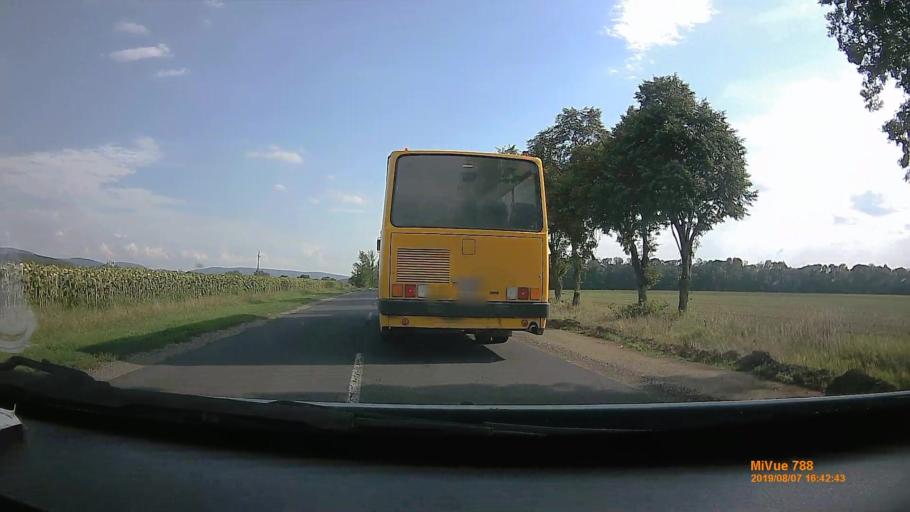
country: HU
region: Borsod-Abauj-Zemplen
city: Abaujszanto
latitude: 48.3666
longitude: 21.2158
